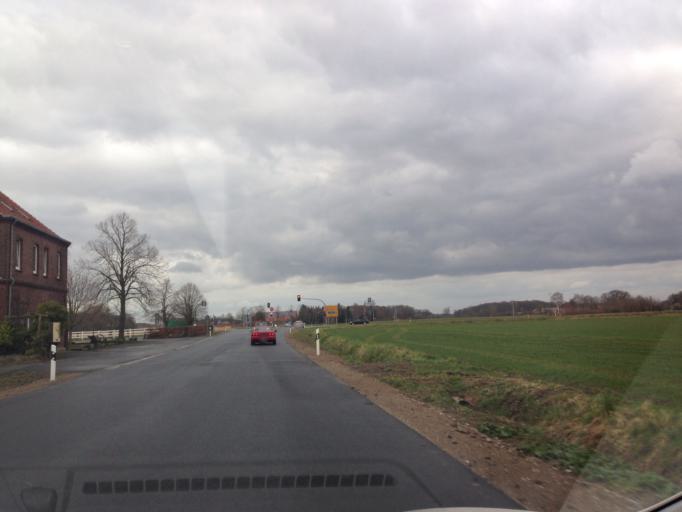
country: DE
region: North Rhine-Westphalia
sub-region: Regierungsbezirk Munster
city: Nordkirchen
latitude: 51.7853
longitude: 7.5422
